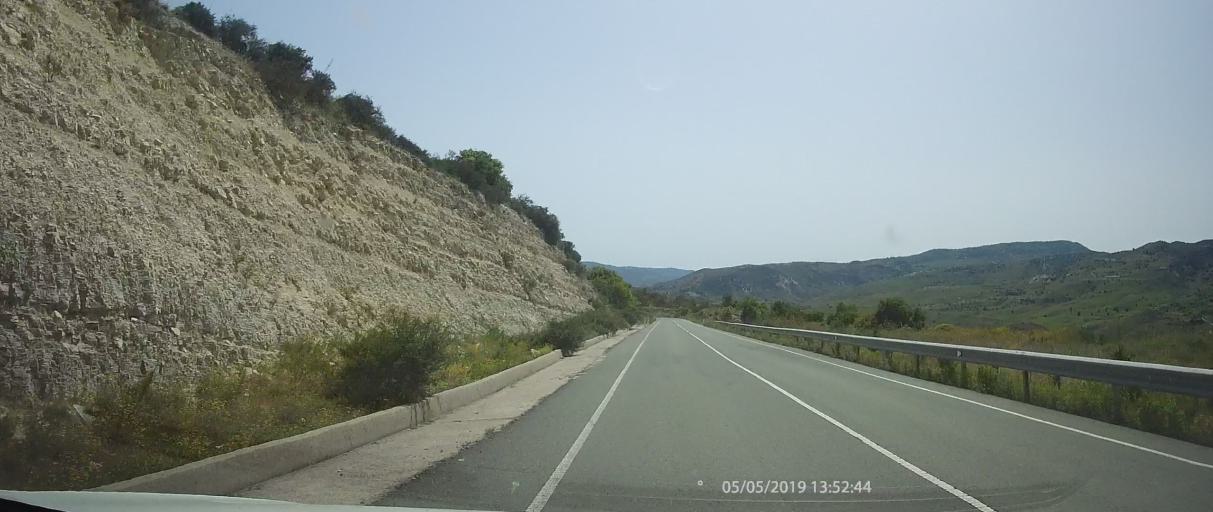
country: CY
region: Limassol
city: Pachna
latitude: 34.8282
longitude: 32.7293
